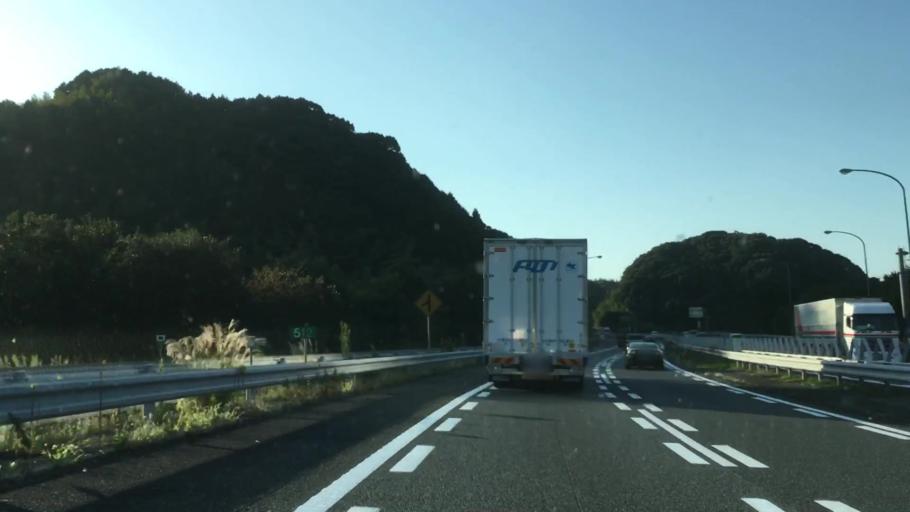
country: JP
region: Yamaguchi
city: Onoda
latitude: 34.1085
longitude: 131.1399
